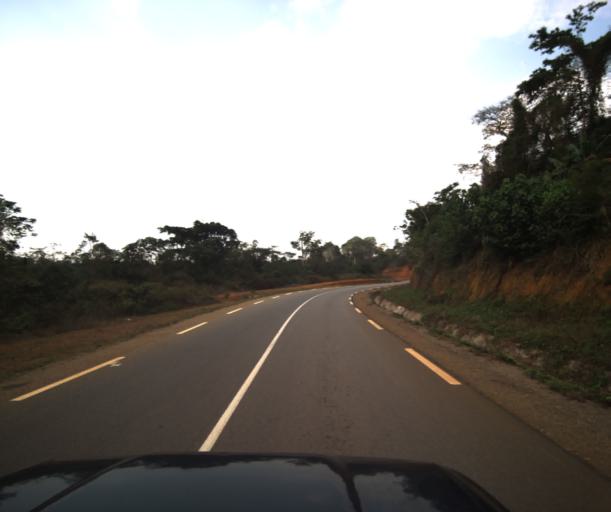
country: CM
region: Centre
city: Mbankomo
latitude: 3.6614
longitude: 11.3419
